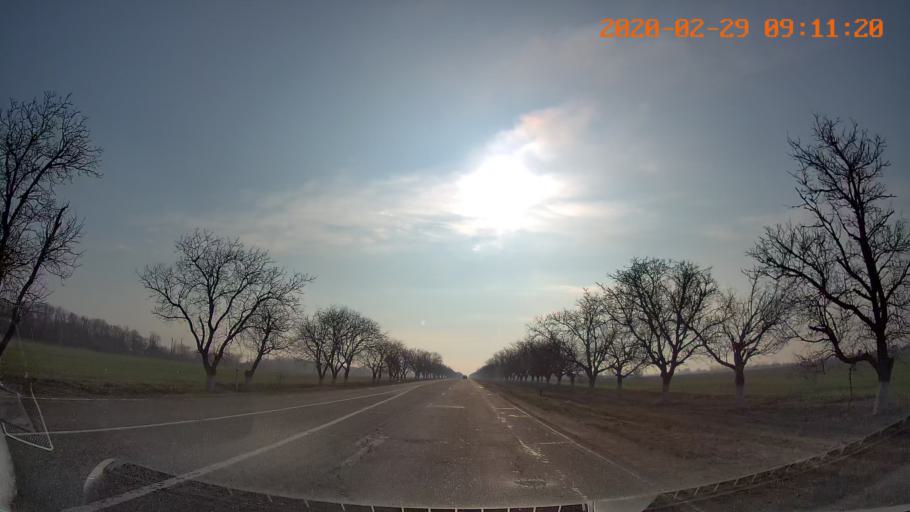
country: MD
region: Telenesti
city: Slobozia
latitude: 46.8360
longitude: 29.7981
